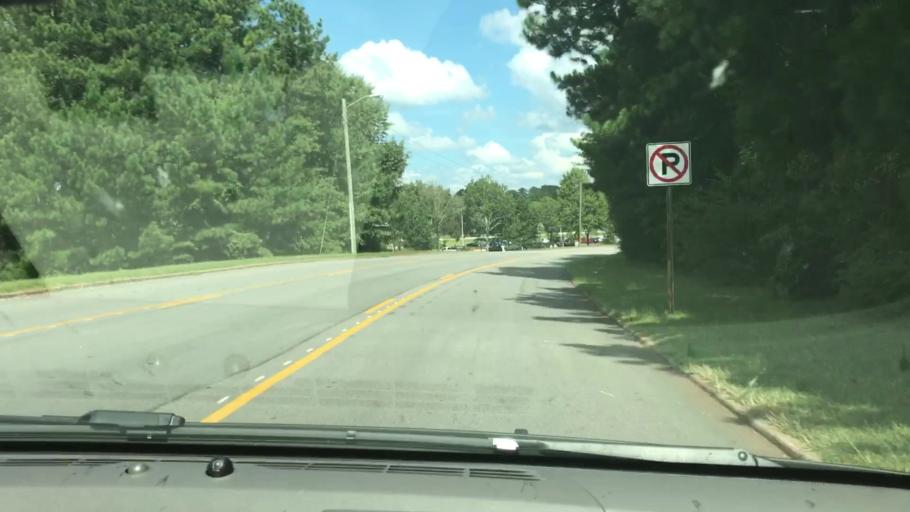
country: US
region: Georgia
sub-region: Troup County
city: La Grange
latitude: 33.0061
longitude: -85.0569
